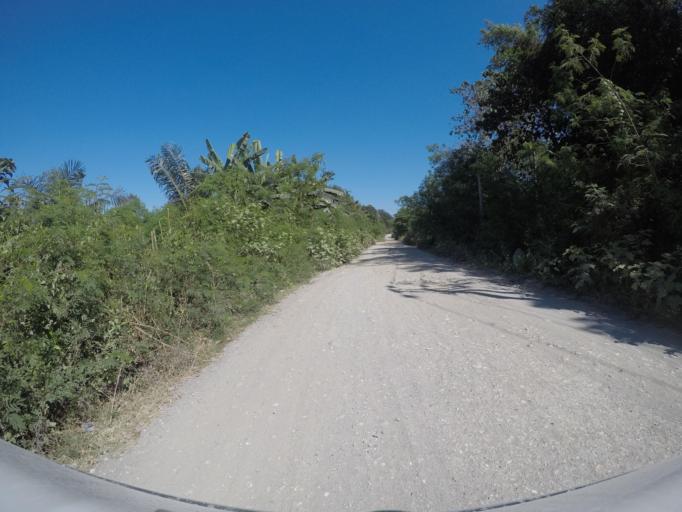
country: TL
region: Viqueque
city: Viqueque
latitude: -8.9742
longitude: 126.0633
